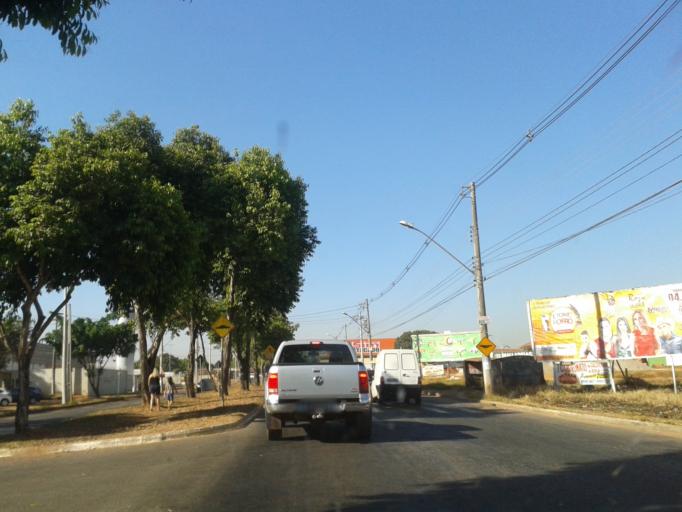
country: BR
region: Goias
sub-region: Goiania
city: Goiania
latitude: -16.6797
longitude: -49.3282
